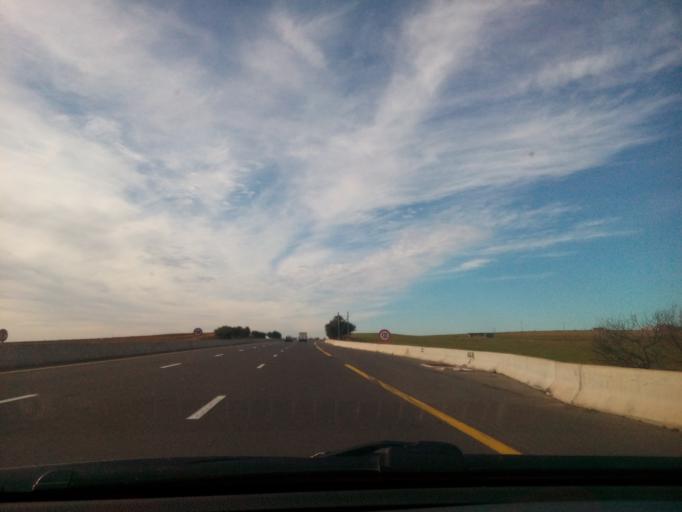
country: DZ
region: Sidi Bel Abbes
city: Sidi Bel Abbes
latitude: 35.1938
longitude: -0.7003
